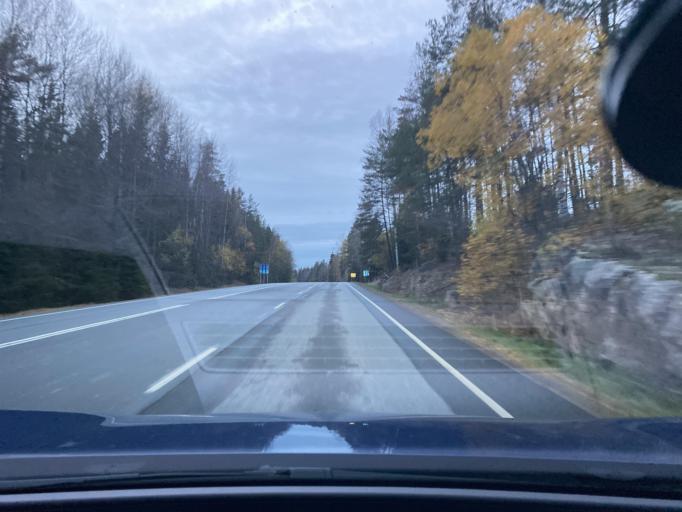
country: FI
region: Uusimaa
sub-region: Helsinki
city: Sammatti
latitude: 60.3860
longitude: 23.8607
